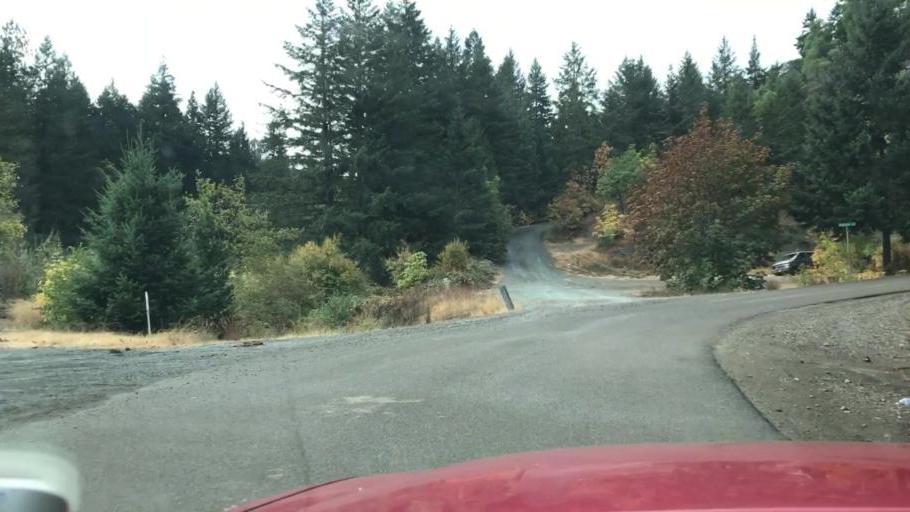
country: US
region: Oregon
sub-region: Douglas County
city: Canyonville
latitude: 42.7635
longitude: -123.3324
